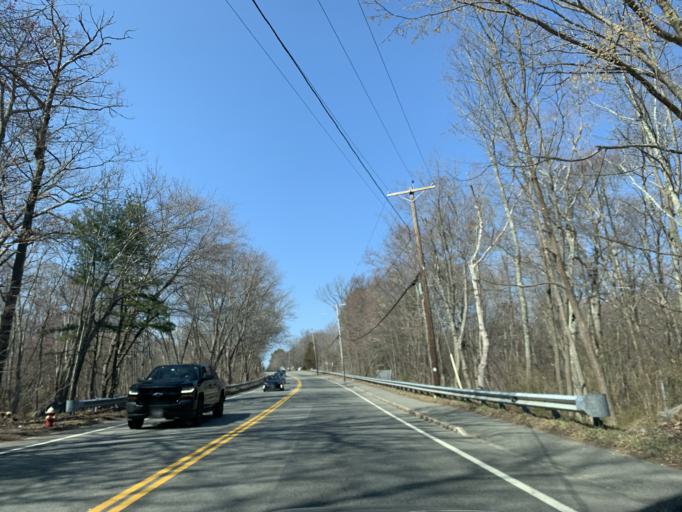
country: US
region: Massachusetts
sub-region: Norfolk County
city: Plainville
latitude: 42.0197
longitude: -71.3070
